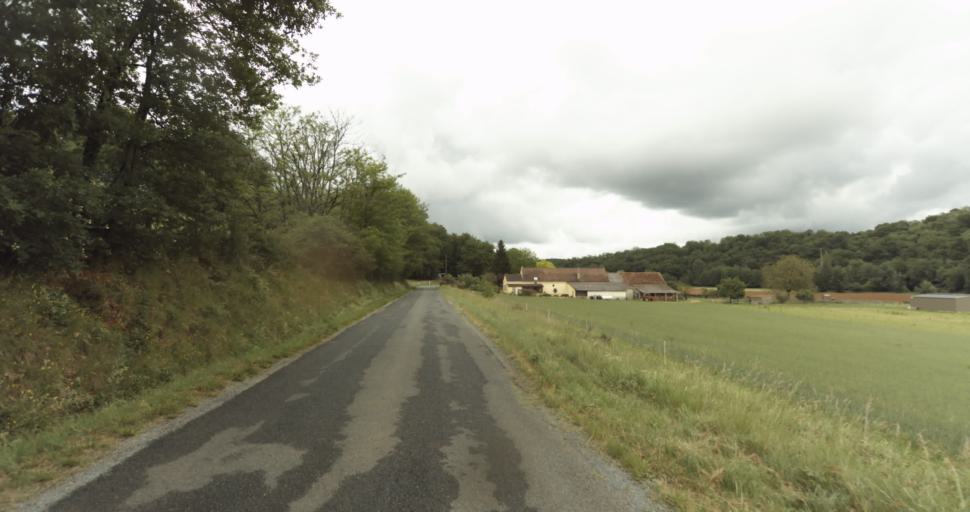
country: FR
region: Aquitaine
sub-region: Departement de la Dordogne
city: Belves
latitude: 44.7595
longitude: 0.8926
